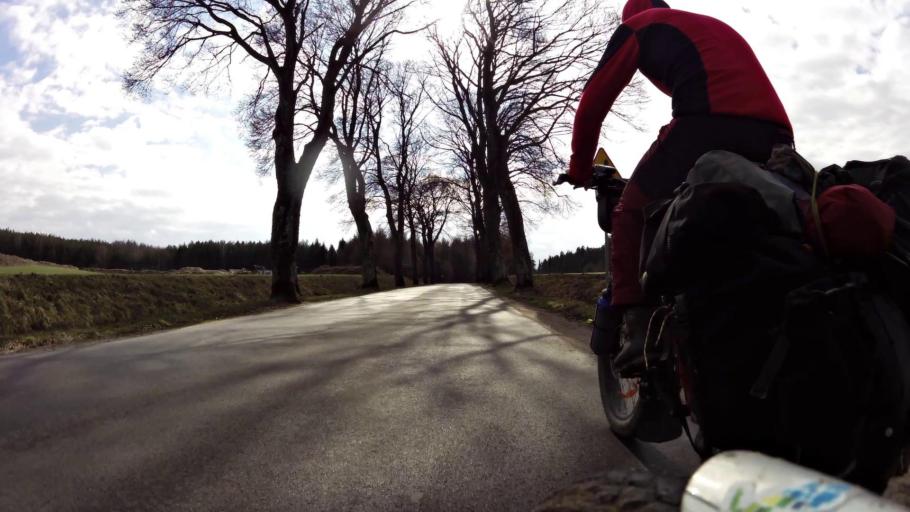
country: PL
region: Pomeranian Voivodeship
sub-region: Powiat bytowski
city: Kolczyglowy
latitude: 54.2088
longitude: 17.2354
